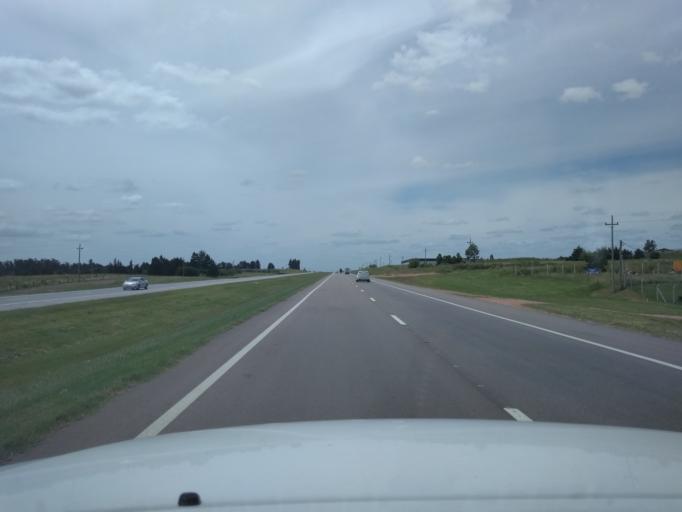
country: UY
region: Canelones
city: Las Piedras
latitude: -34.7100
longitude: -56.2423
